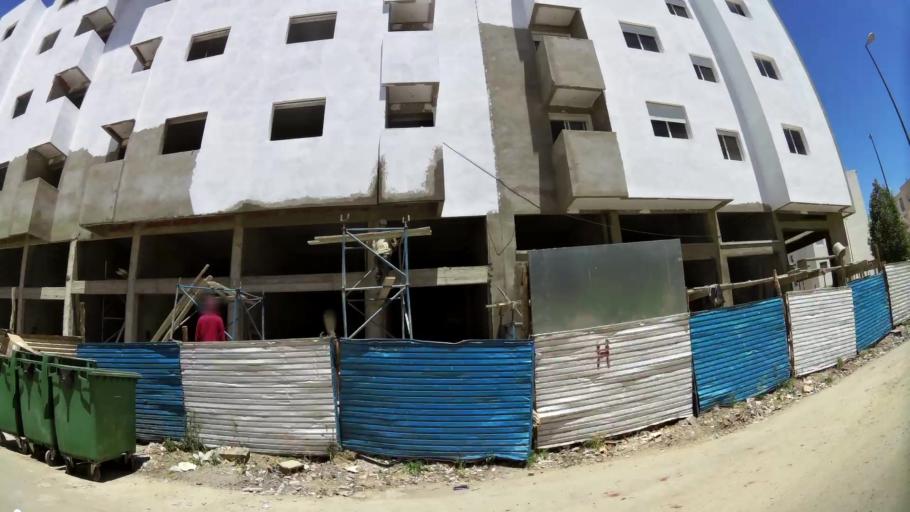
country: MA
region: Meknes-Tafilalet
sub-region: Meknes
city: Meknes
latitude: 33.8612
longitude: -5.5624
